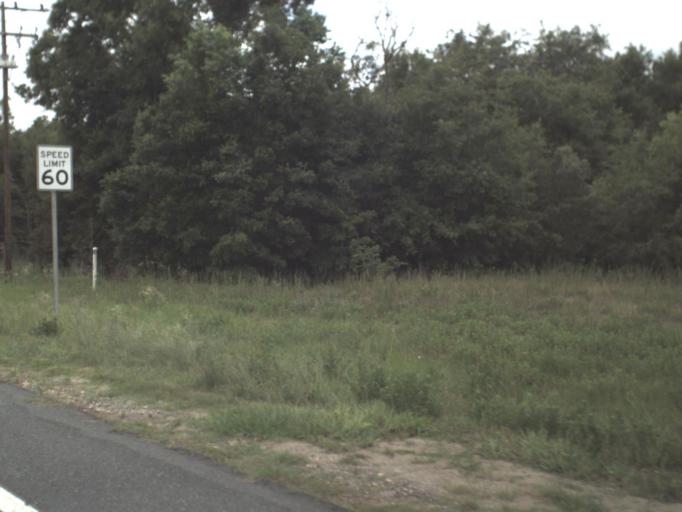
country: US
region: Florida
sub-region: Levy County
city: Williston Highlands
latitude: 29.2169
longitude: -82.4404
